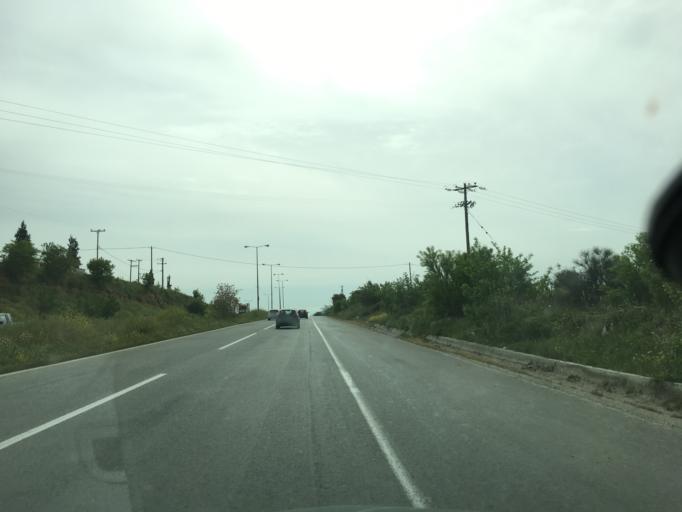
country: GR
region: Thessaly
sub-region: Nomos Magnisias
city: Nea Ionia
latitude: 39.3828
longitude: 22.8520
